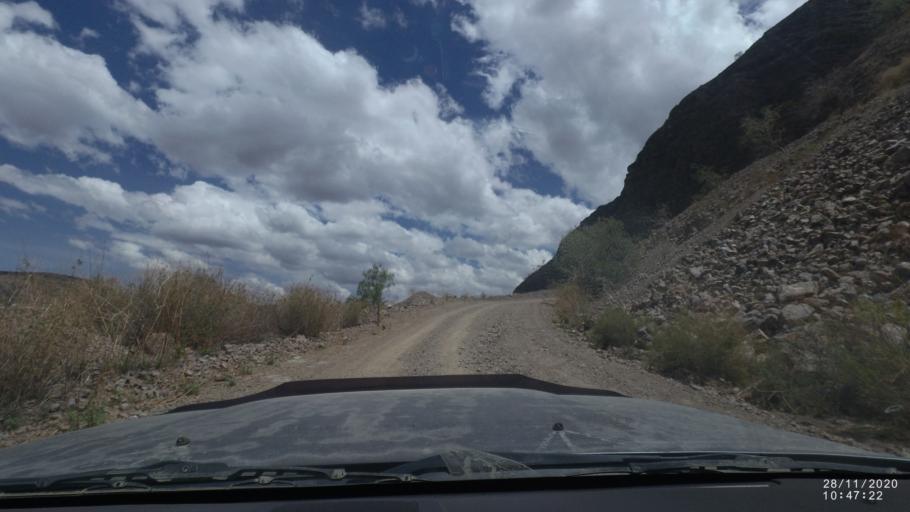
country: BO
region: Cochabamba
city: Capinota
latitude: -17.7852
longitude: -66.1252
